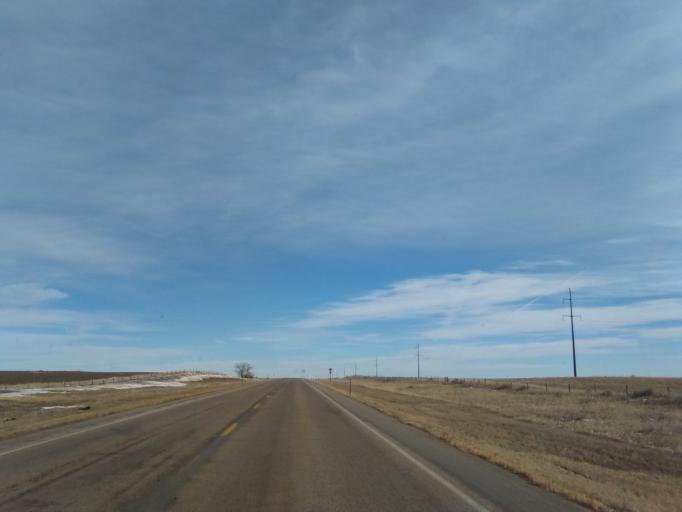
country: US
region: Wyoming
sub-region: Laramie County
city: Pine Bluffs
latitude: 41.4233
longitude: -104.3966
